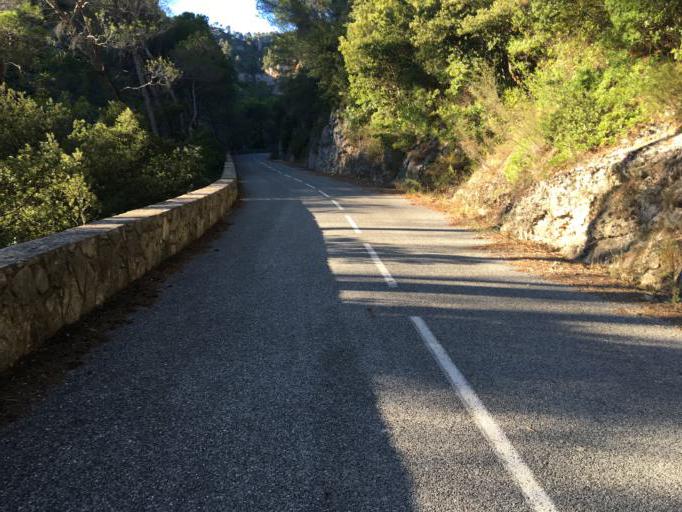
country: FR
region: Provence-Alpes-Cote d'Azur
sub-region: Departement du Var
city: Flayosc
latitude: 43.5849
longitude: 6.4254
